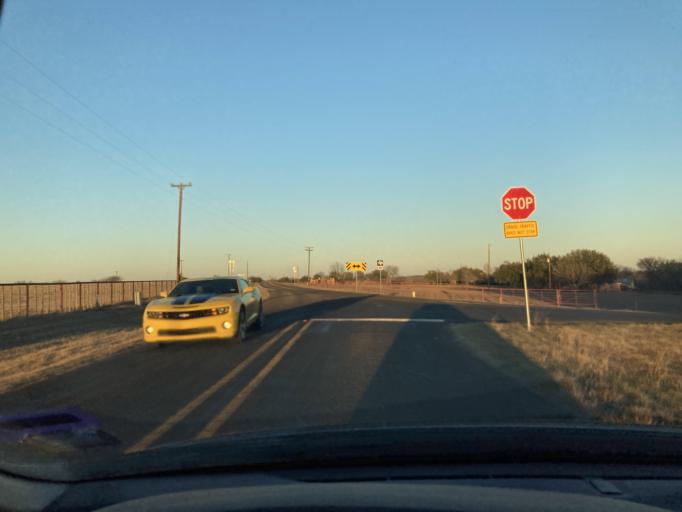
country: US
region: Texas
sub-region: Ellis County
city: Waxahachie
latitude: 32.3439
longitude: -96.8743
